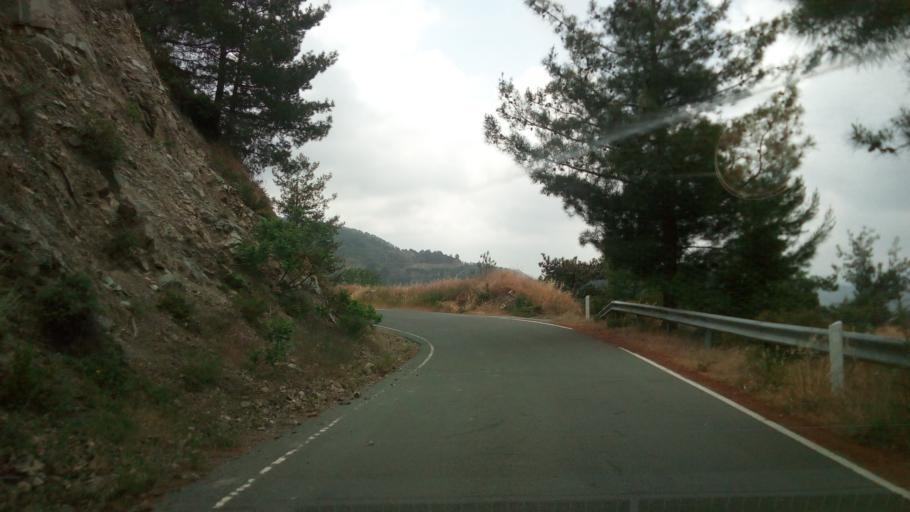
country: CY
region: Limassol
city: Pelendri
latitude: 34.8938
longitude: 32.9958
